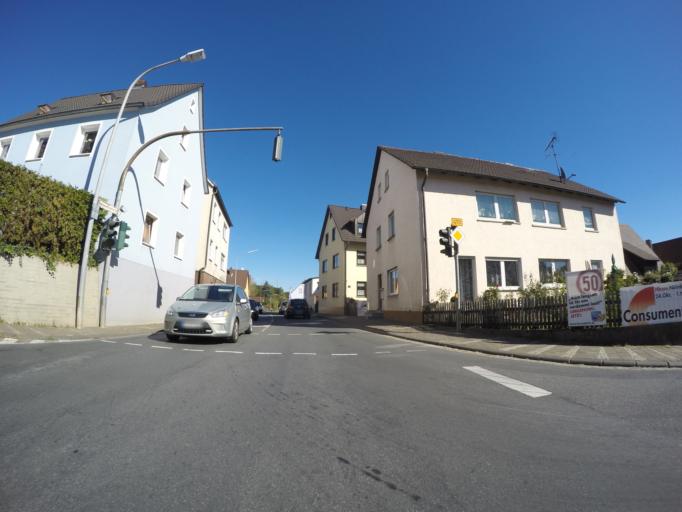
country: DE
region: Bavaria
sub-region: Upper Franconia
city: Wiesenthau
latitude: 49.7207
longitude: 11.1133
